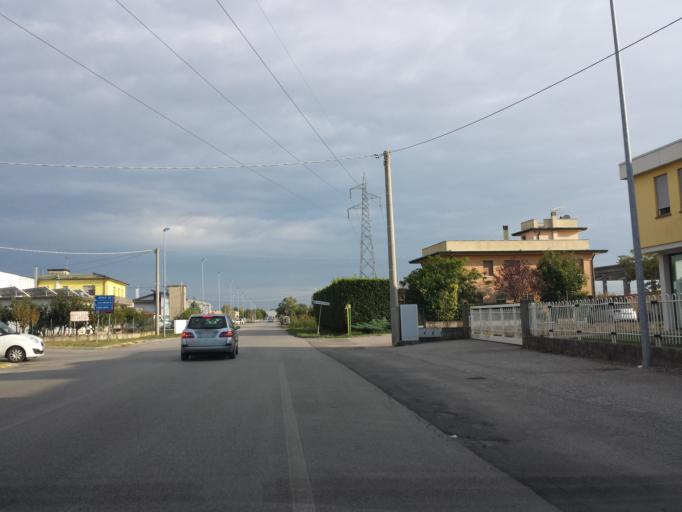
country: IT
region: Veneto
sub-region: Provincia di Rovigo
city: Sant'Apollinare
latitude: 45.0428
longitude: 11.7985
